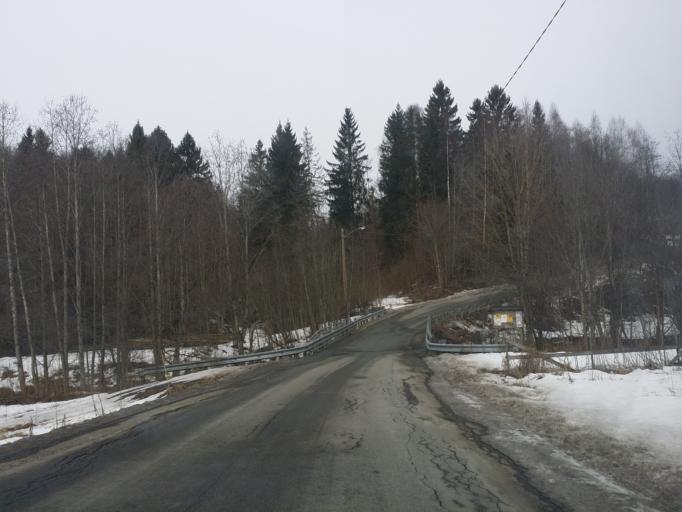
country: NO
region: Buskerud
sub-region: Lier
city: Tranby
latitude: 59.8492
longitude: 10.2483
